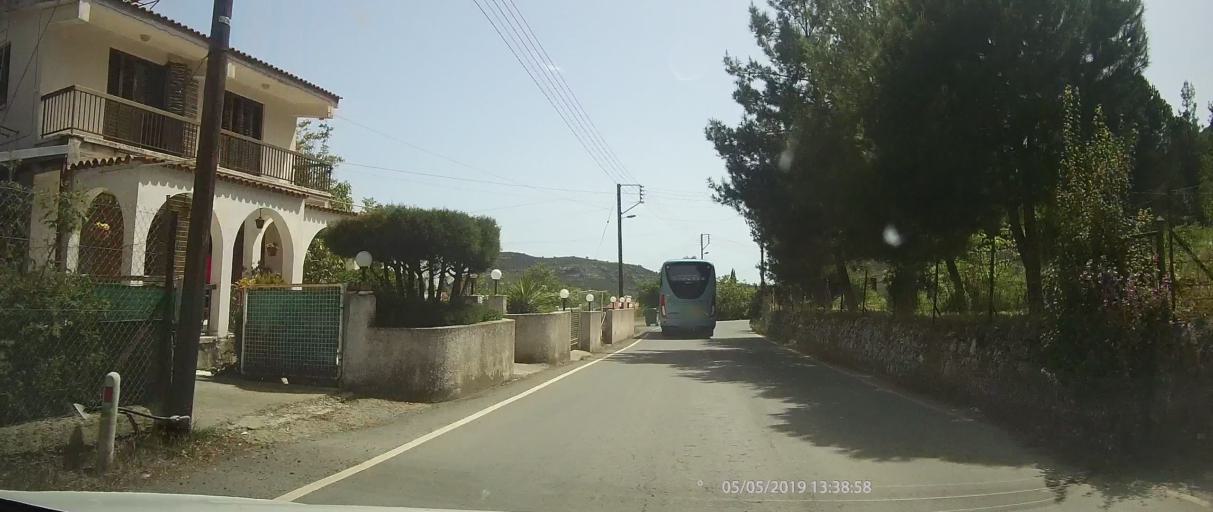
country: CY
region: Limassol
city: Pachna
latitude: 34.8725
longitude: 32.8325
